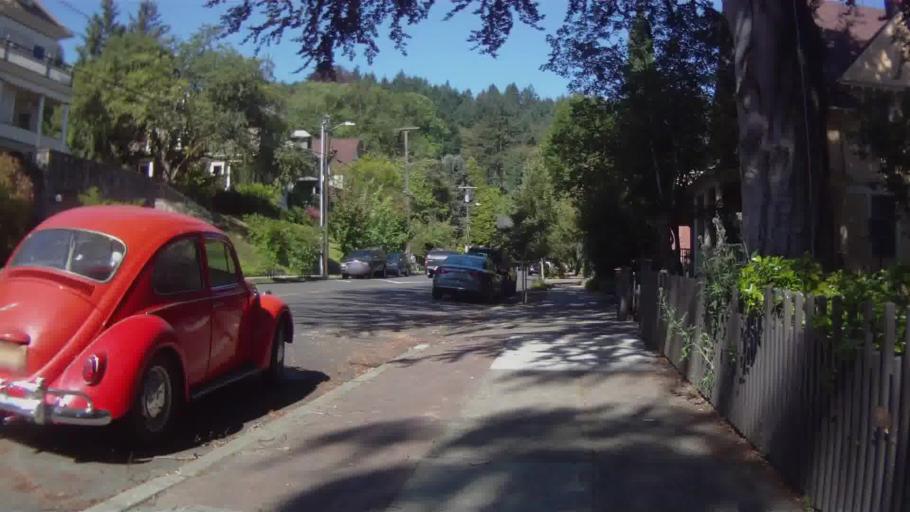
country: US
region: Oregon
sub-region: Multnomah County
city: Portland
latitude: 45.5359
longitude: -122.7149
